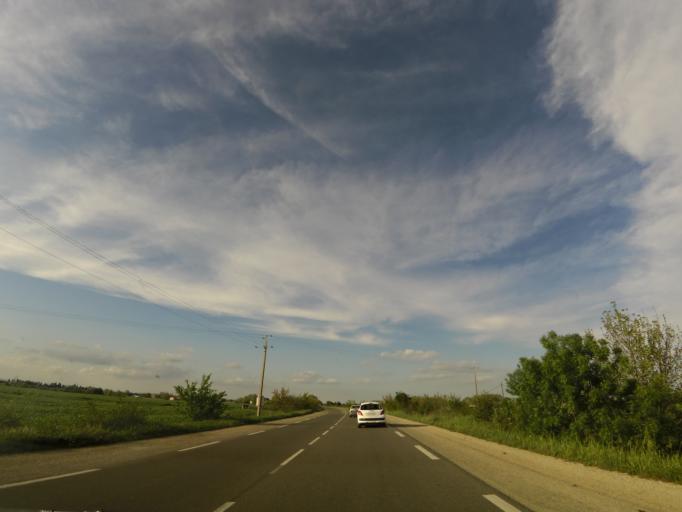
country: FR
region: Languedoc-Roussillon
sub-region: Departement de l'Herault
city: Saint-Just
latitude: 43.6417
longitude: 4.1382
